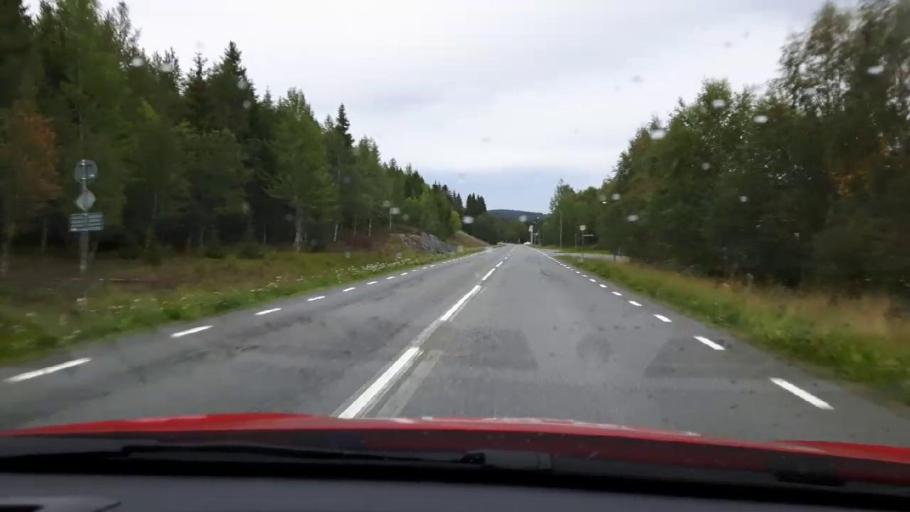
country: SE
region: Jaemtland
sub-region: Are Kommun
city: Jarpen
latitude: 63.3938
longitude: 13.3839
